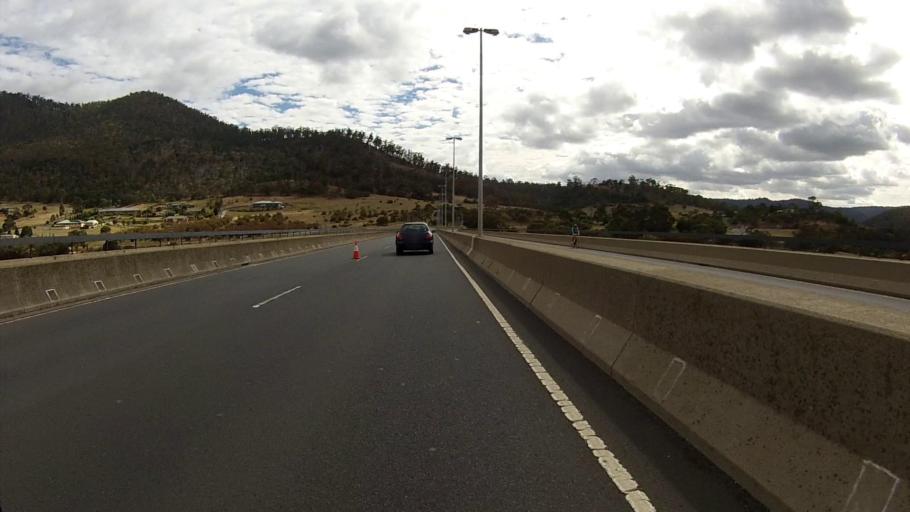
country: AU
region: Tasmania
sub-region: Glenorchy
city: Lutana
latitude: -42.8157
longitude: 147.3093
